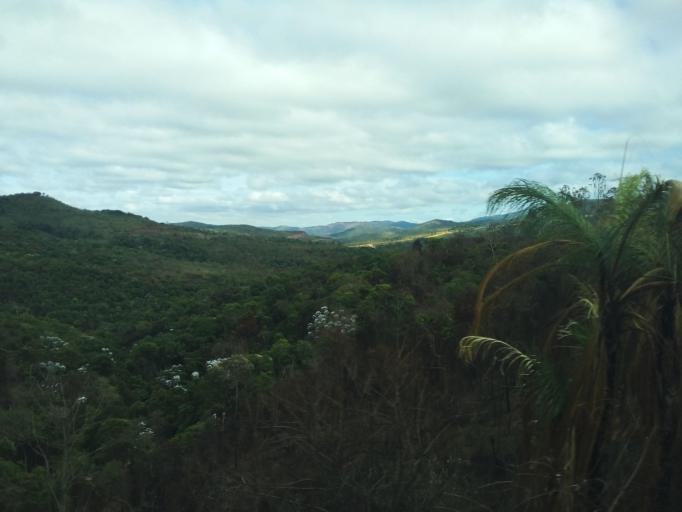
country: BR
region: Minas Gerais
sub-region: Caete
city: Caete
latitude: -19.9124
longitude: -43.6997
